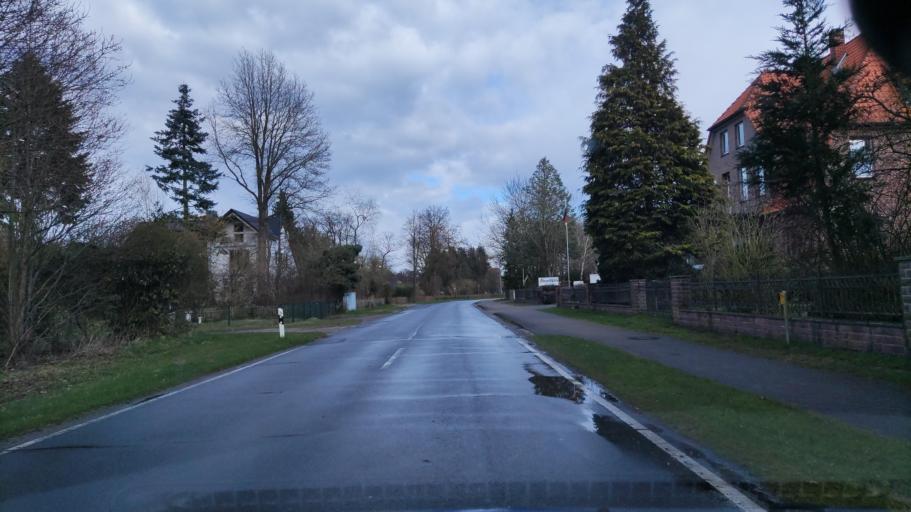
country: DE
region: Lower Saxony
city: Hermannsburg
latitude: 52.8340
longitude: 10.1297
